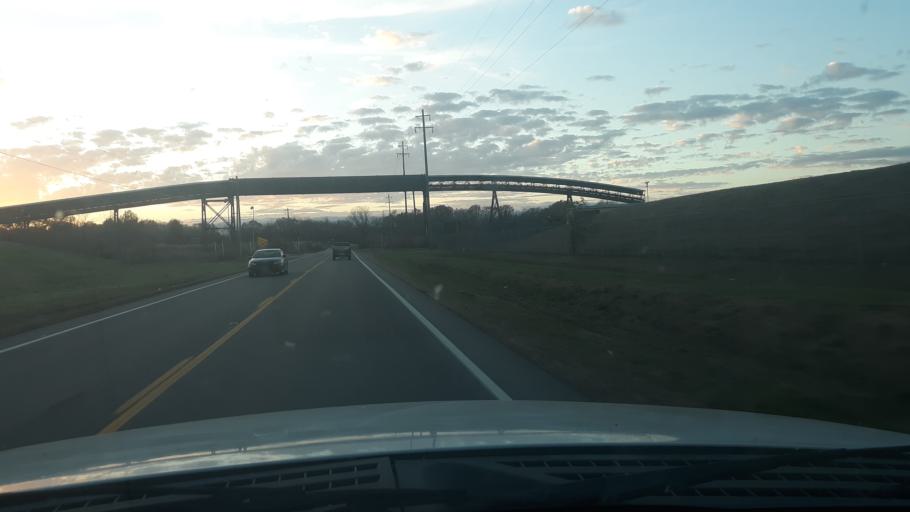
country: US
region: Illinois
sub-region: Saline County
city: Harrisburg
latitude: 37.8347
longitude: -88.5821
